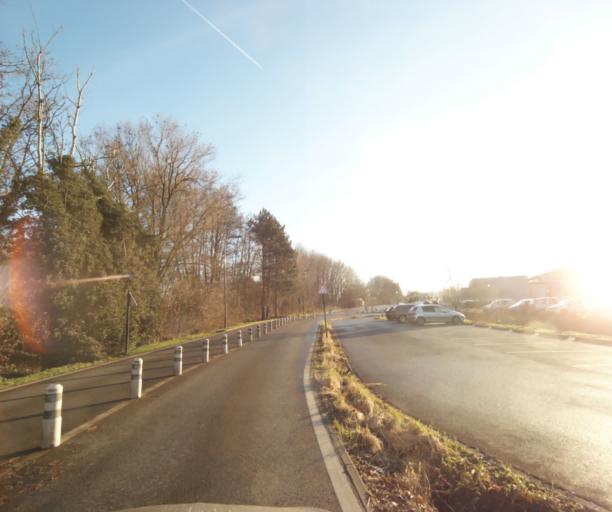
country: FR
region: Nord-Pas-de-Calais
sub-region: Departement du Nord
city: Famars
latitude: 50.3269
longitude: 3.5174
